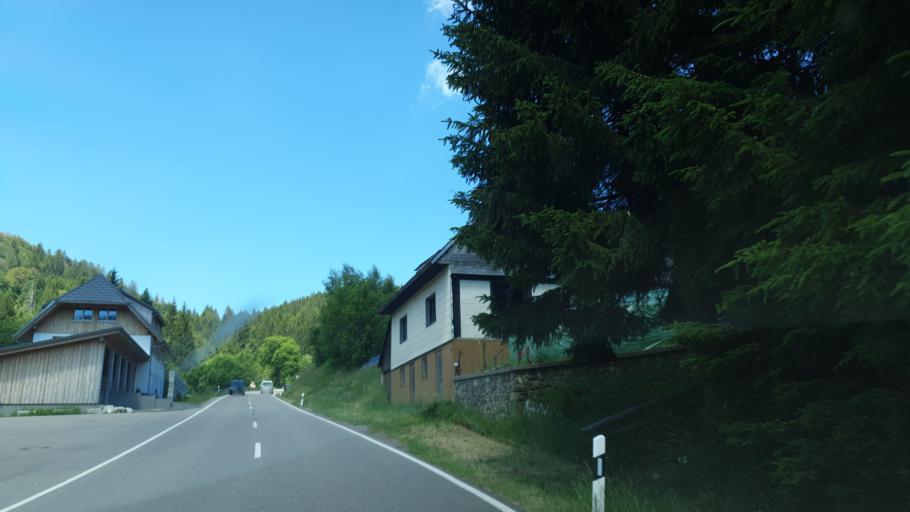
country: DE
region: Baden-Wuerttemberg
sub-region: Freiburg Region
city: Todtnau
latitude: 47.8621
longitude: 7.9192
